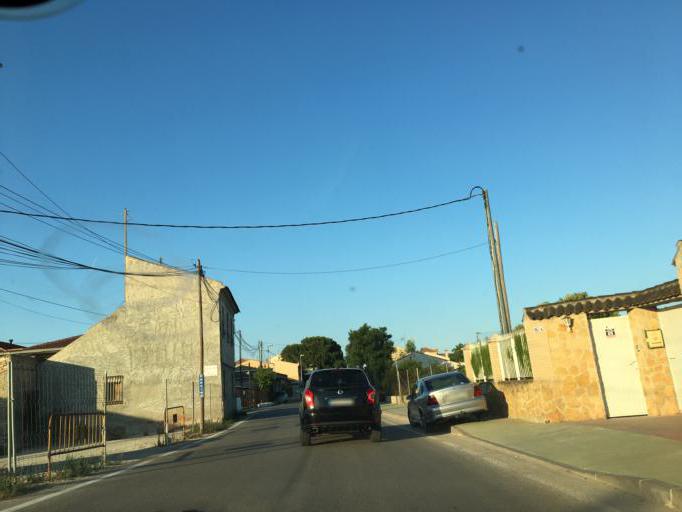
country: ES
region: Murcia
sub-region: Murcia
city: Santomera
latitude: 38.0088
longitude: -1.0736
